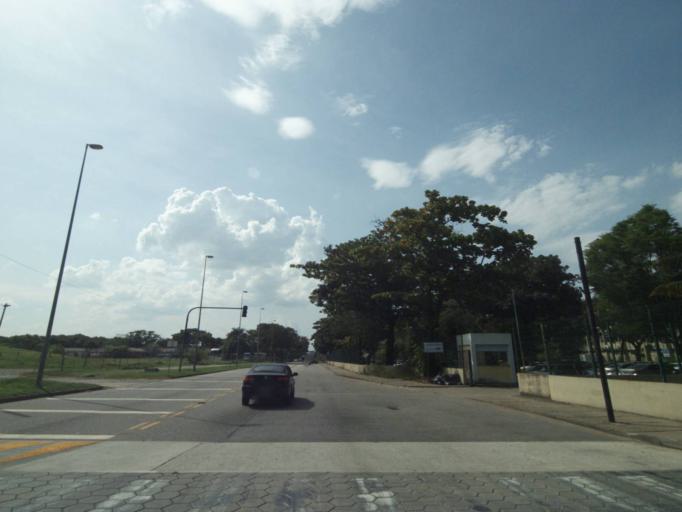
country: BR
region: Rio de Janeiro
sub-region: Rio De Janeiro
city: Rio de Janeiro
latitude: -22.8580
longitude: -43.2339
